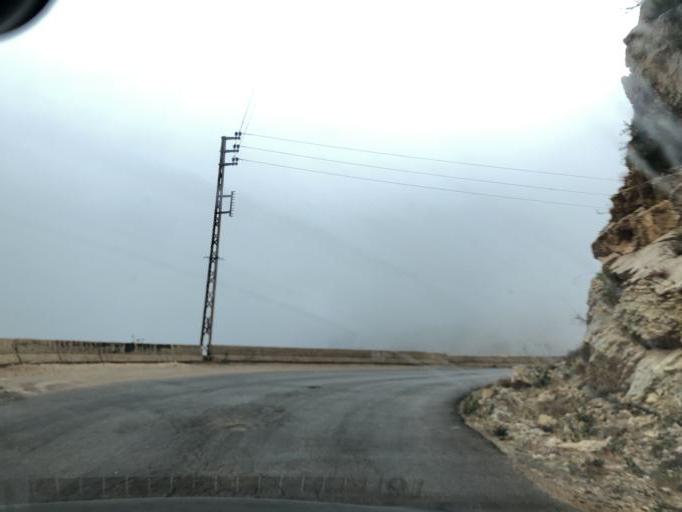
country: LB
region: Liban-Nord
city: Bcharre
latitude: 34.1246
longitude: 35.8950
